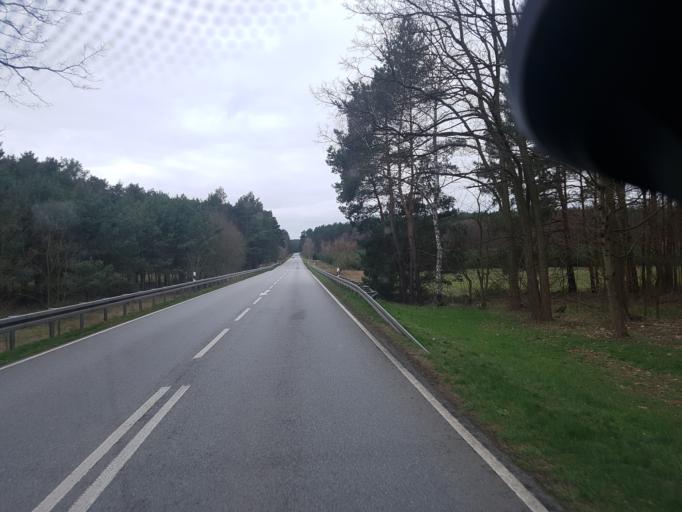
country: DE
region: Brandenburg
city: Neu Zauche
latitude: 51.9970
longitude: 14.0266
